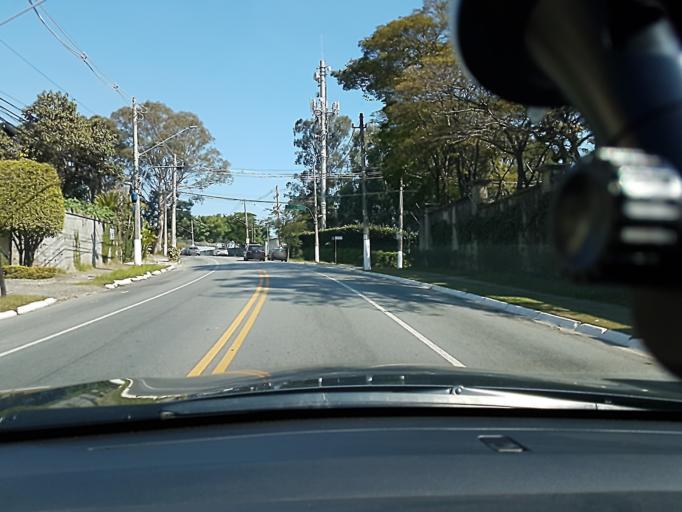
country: BR
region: Sao Paulo
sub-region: Taboao Da Serra
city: Taboao da Serra
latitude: -23.6092
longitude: -46.7128
